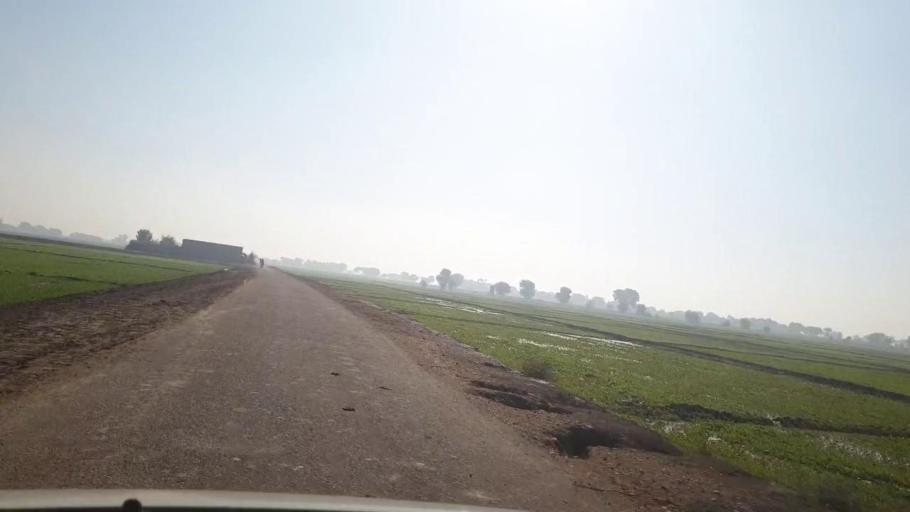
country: PK
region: Sindh
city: Dadu
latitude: 26.6404
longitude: 67.8284
